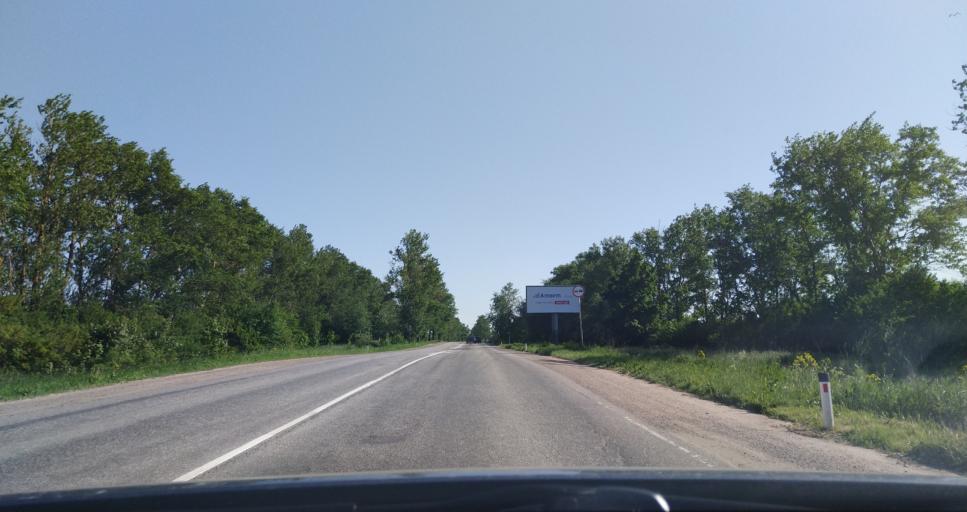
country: RU
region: Leningrad
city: Taytsy
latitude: 59.6772
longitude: 30.1098
